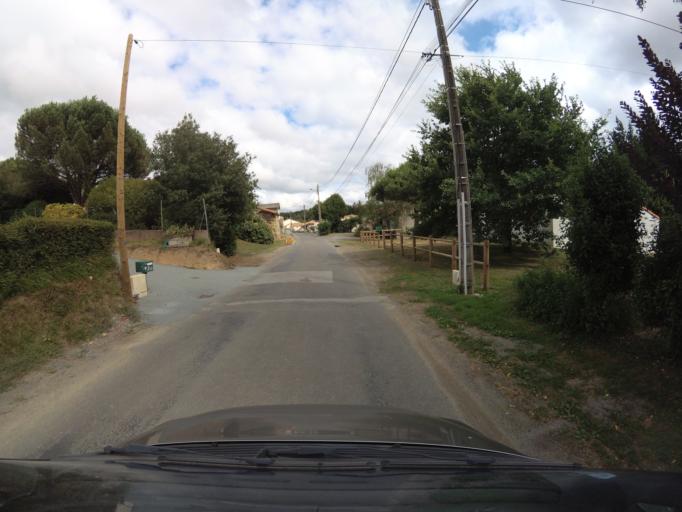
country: FR
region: Pays de la Loire
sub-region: Departement de la Loire-Atlantique
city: La Limouziniere
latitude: 47.0166
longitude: -1.5635
